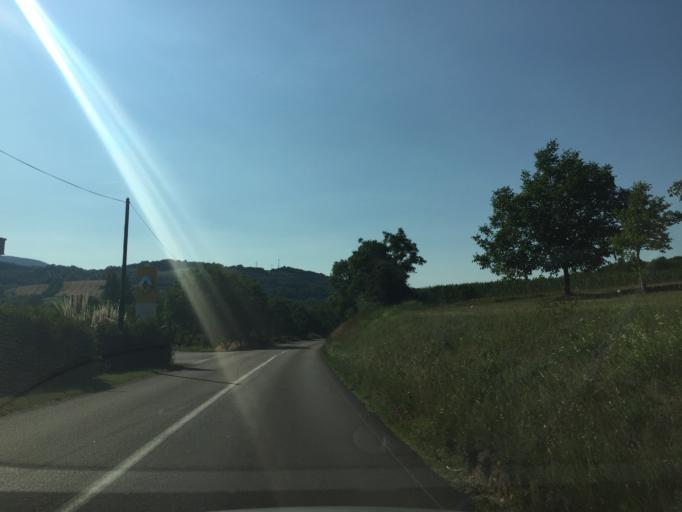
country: FR
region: Rhone-Alpes
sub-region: Departement de la Drome
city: Saint-Laurent-en-Royans
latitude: 45.0330
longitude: 5.3094
